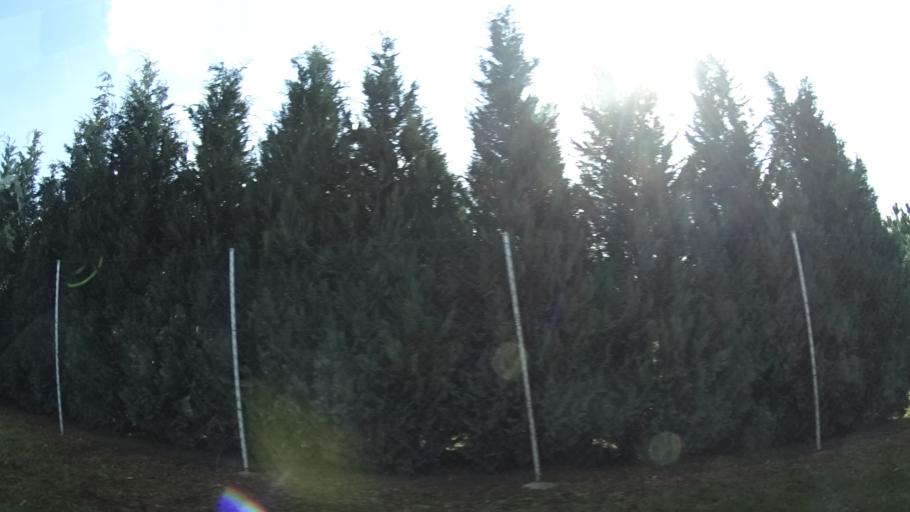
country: DE
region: Saxony-Anhalt
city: Leissling
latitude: 51.1574
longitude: 11.8991
